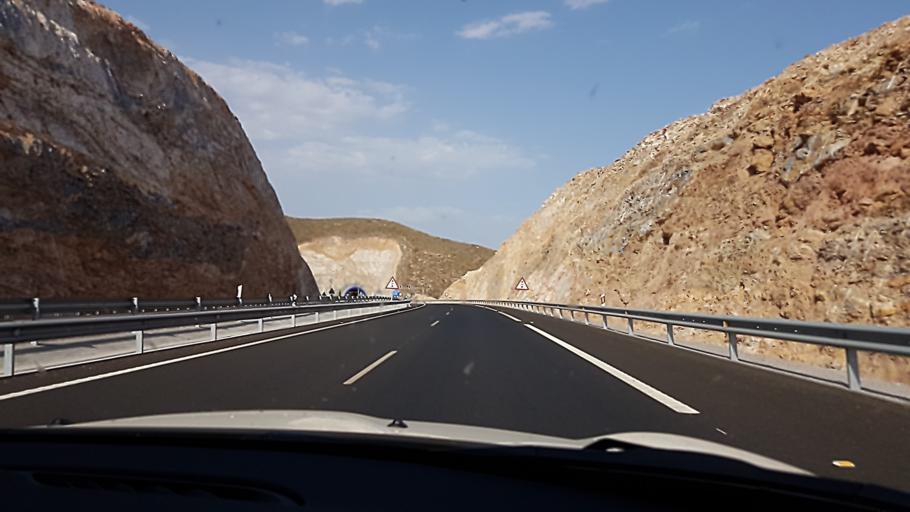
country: ES
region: Andalusia
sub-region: Provincia de Granada
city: Gualchos
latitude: 36.7174
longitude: -3.3796
